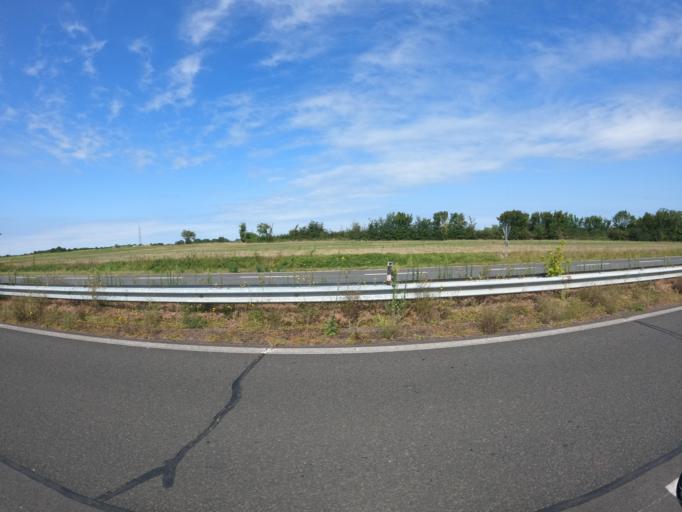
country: FR
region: Poitou-Charentes
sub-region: Departement des Deux-Sevres
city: Frontenay-Rohan-Rohan
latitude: 46.2538
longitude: -0.5481
